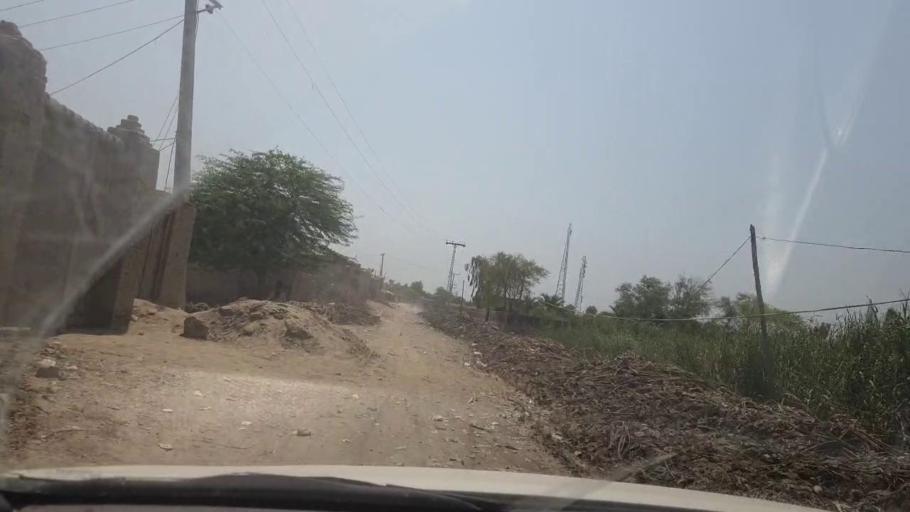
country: PK
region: Sindh
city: Lakhi
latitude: 27.8600
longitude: 68.7134
